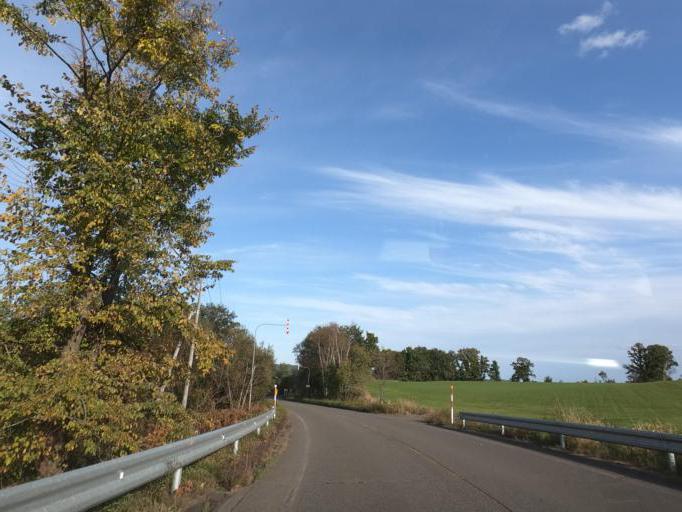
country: JP
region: Hokkaido
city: Obihiro
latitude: 42.5601
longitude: 143.3489
